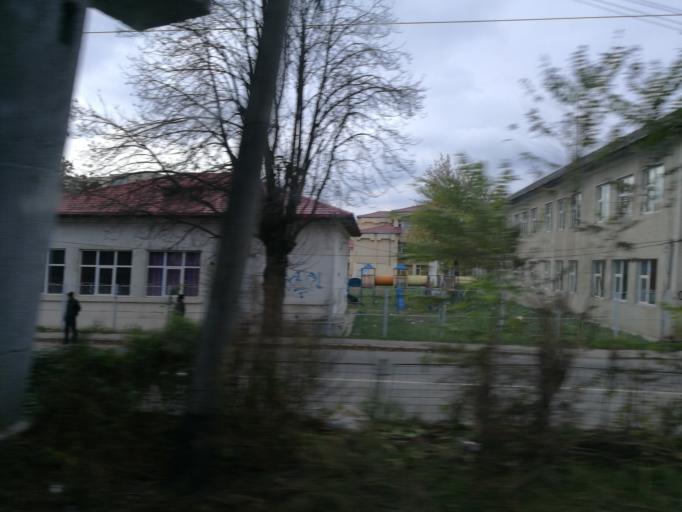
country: RO
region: Bacau
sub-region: Municipiul Bacau
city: Bacau
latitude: 46.5441
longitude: 26.9155
